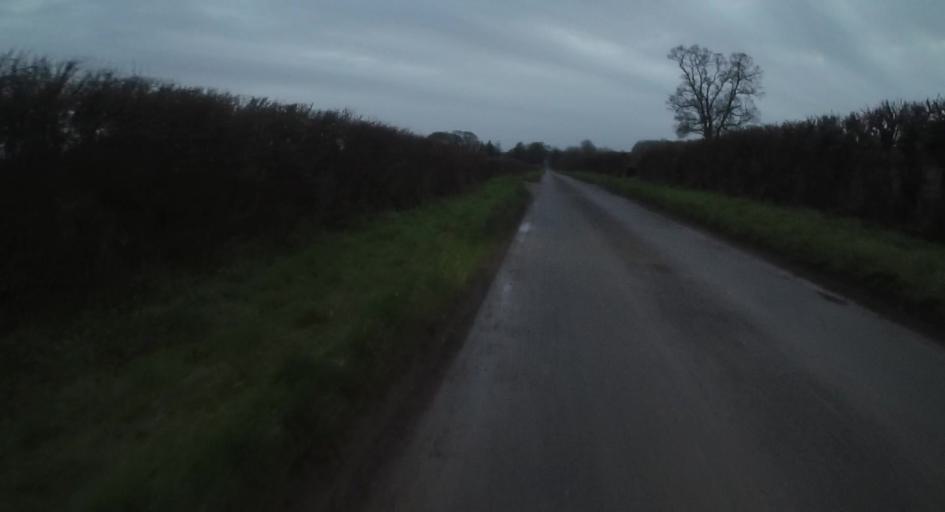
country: GB
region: England
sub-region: Hampshire
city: Overton
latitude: 51.2139
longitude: -1.2981
